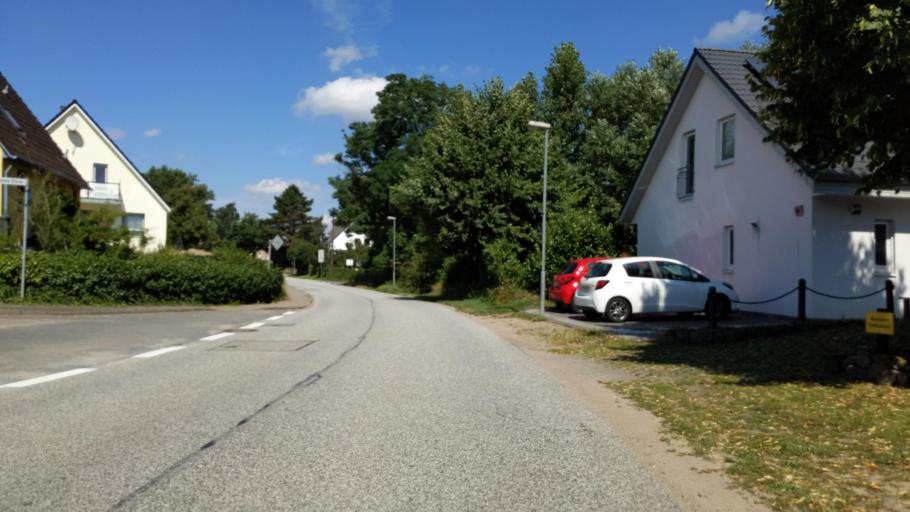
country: DE
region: Schleswig-Holstein
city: Krummesse
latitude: 53.8083
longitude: 10.6843
